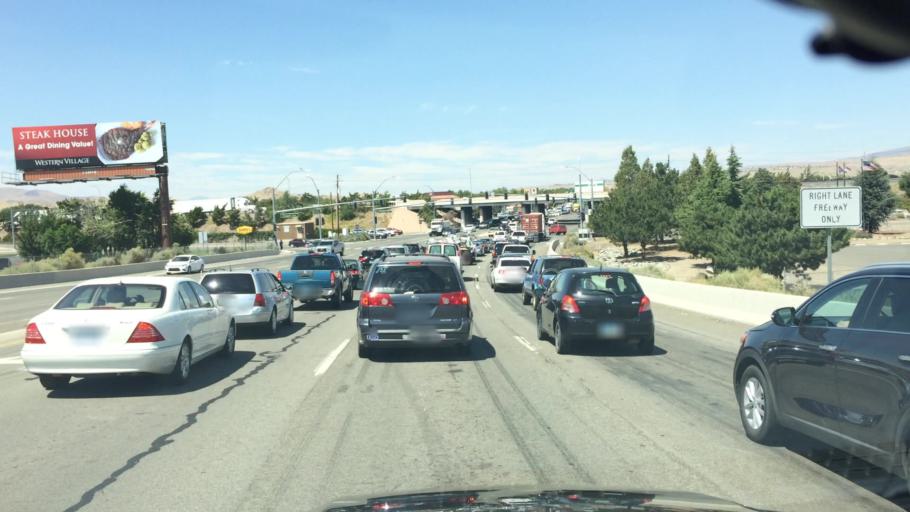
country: US
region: Nevada
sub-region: Washoe County
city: Sparks
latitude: 39.5315
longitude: -119.7395
